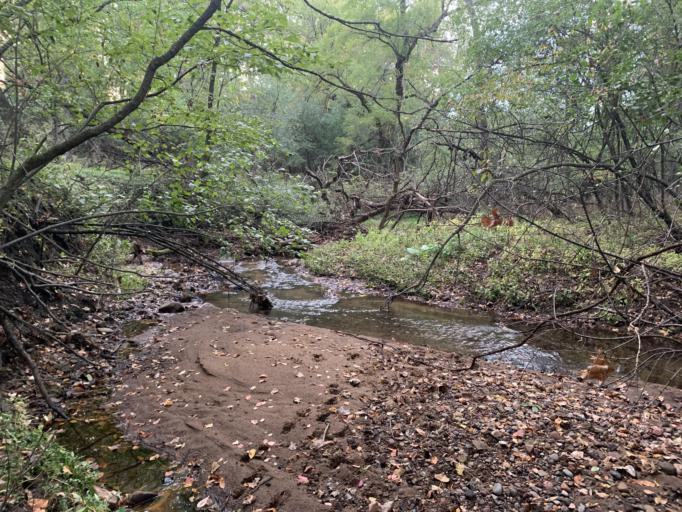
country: US
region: Wisconsin
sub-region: Dunn County
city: Menomonie
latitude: 44.8675
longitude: -91.9331
